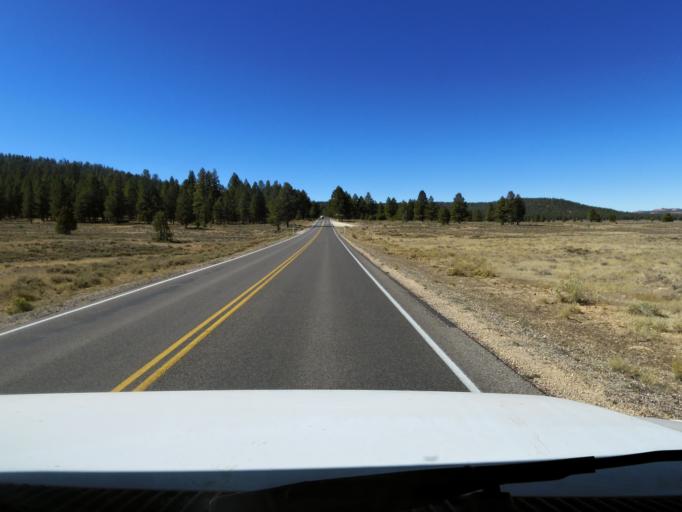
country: US
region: Utah
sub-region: Garfield County
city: Panguitch
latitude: 37.6070
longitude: -112.1893
